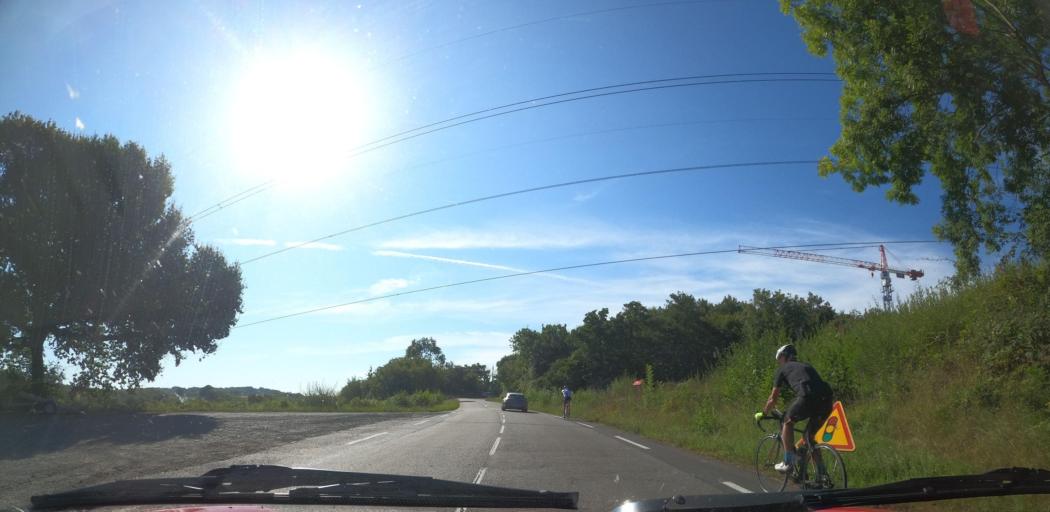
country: FR
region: Aquitaine
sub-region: Departement des Pyrenees-Atlantiques
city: Saint-Pee-sur-Nivelle
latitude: 43.3848
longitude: -1.5420
